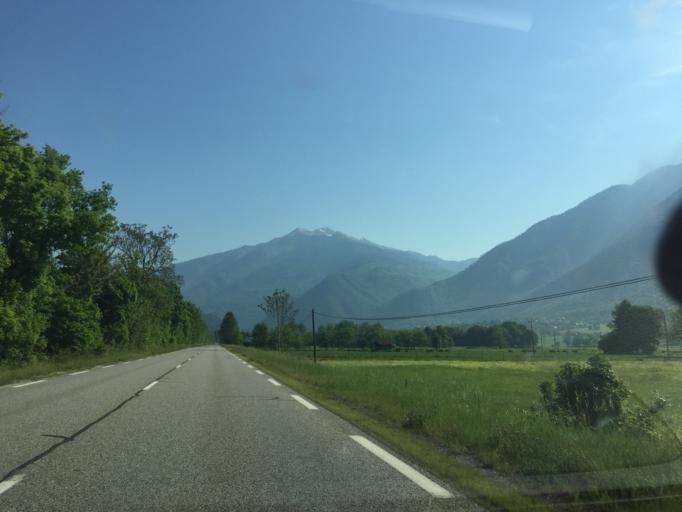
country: FR
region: Rhone-Alpes
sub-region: Departement de la Savoie
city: Aiton
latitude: 45.4818
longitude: 6.2927
